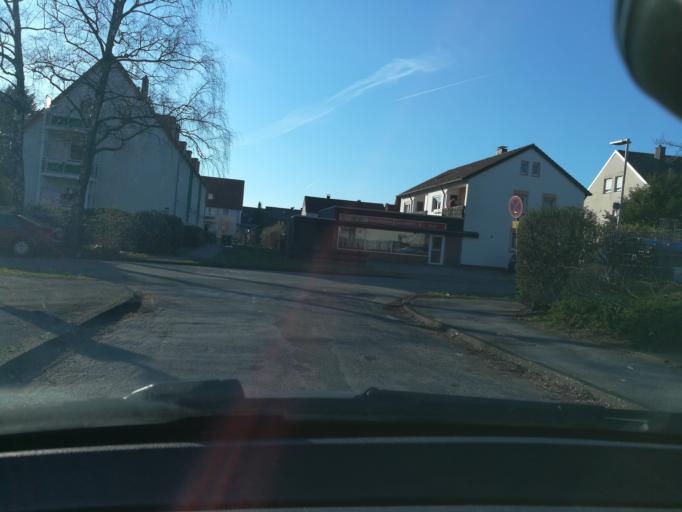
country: DE
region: North Rhine-Westphalia
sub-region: Regierungsbezirk Detmold
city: Oerlinghausen
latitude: 51.9504
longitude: 8.5797
